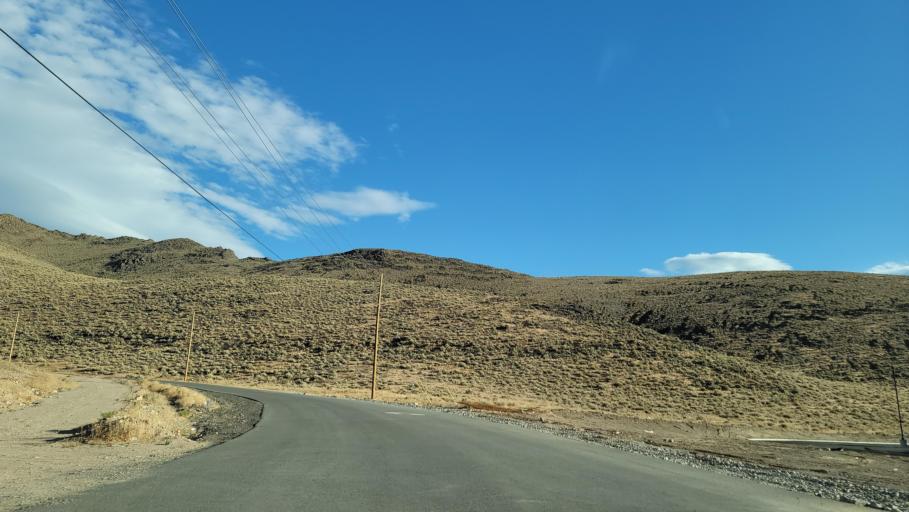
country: US
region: Nevada
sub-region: Washoe County
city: Spanish Springs
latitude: 39.5546
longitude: -119.5264
